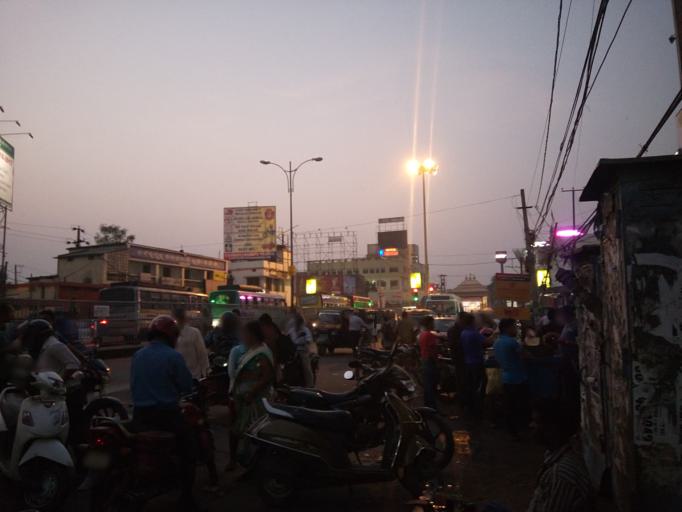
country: IN
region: Odisha
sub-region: Cuttack
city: Cuttack
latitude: 20.4592
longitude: 85.8818
